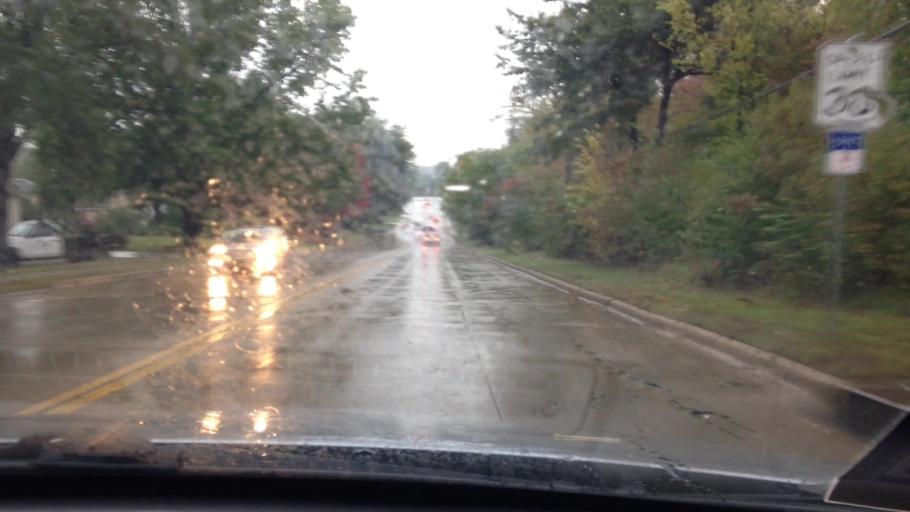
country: US
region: Kansas
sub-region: Leavenworth County
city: Leavenworth
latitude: 39.2851
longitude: -94.9090
